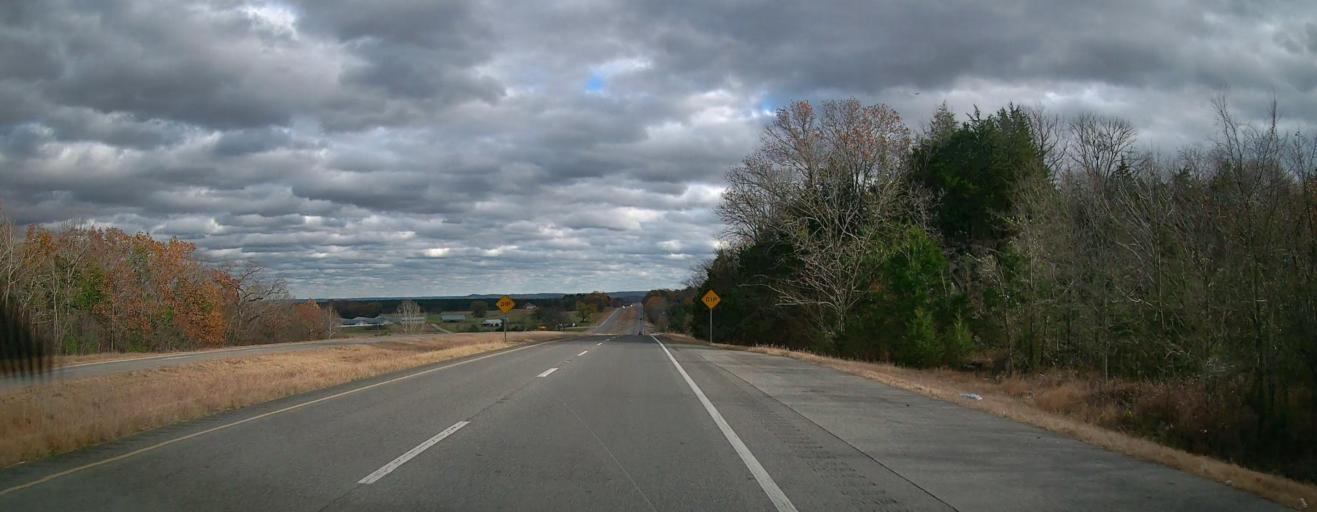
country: US
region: Alabama
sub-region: Morgan County
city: Danville
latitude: 34.3968
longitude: -87.1252
